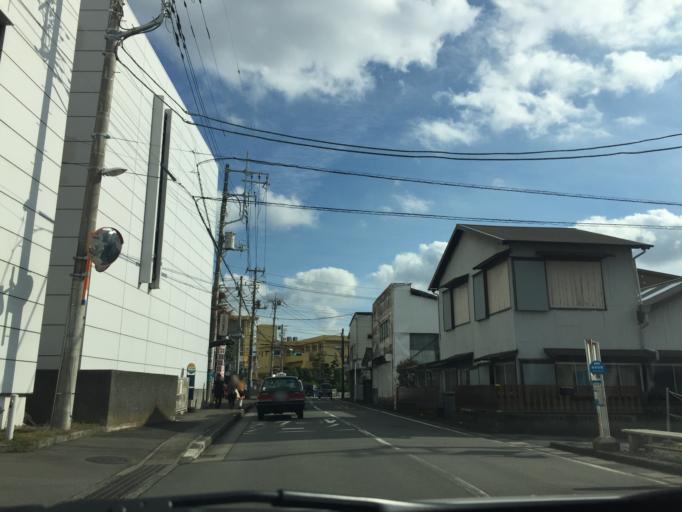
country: JP
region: Shizuoka
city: Mishima
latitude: 35.1374
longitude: 138.8968
